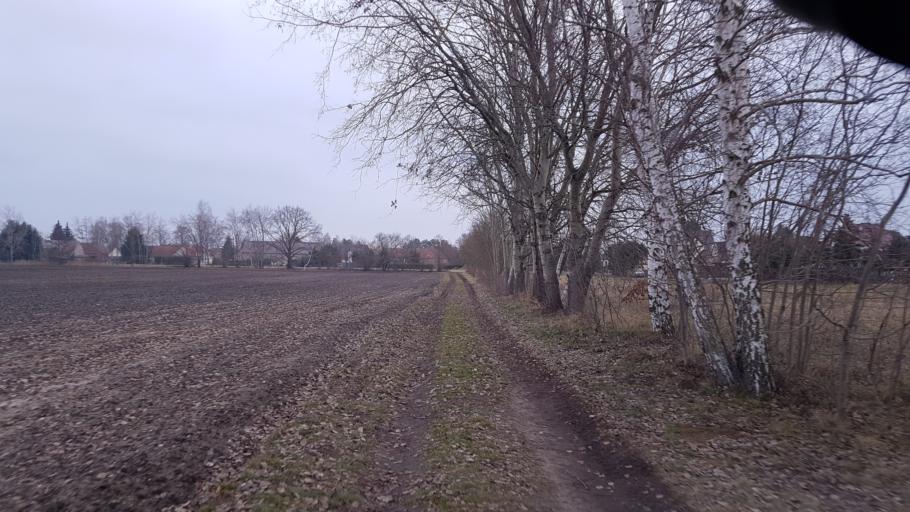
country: DE
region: Brandenburg
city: Schonborn
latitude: 51.5997
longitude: 13.4985
